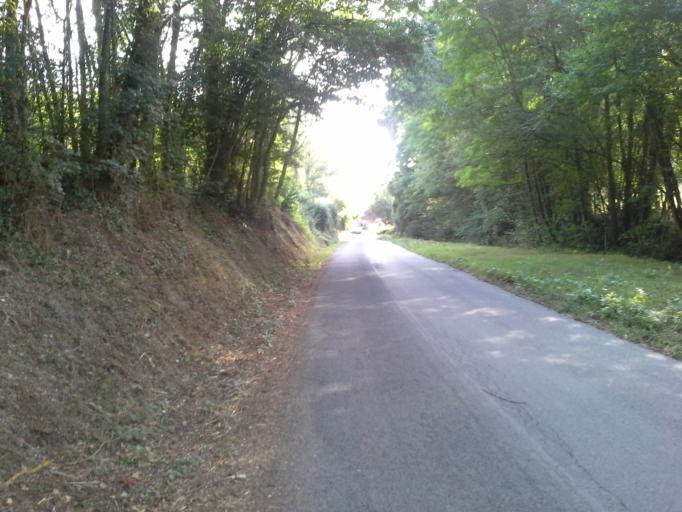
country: FR
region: Centre
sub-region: Departement du Loir-et-Cher
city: Villiers-sur-Loir
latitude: 47.8135
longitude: 0.9852
